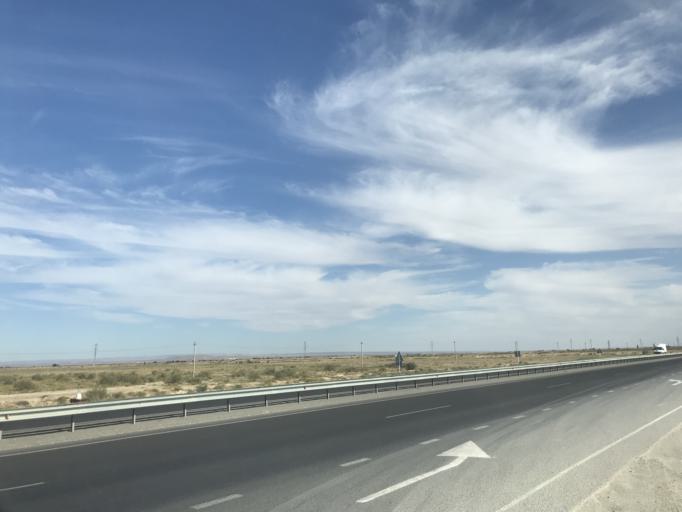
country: KZ
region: Qyzylorda
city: Zhangaqorghan
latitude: 44.0127
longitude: 67.1999
